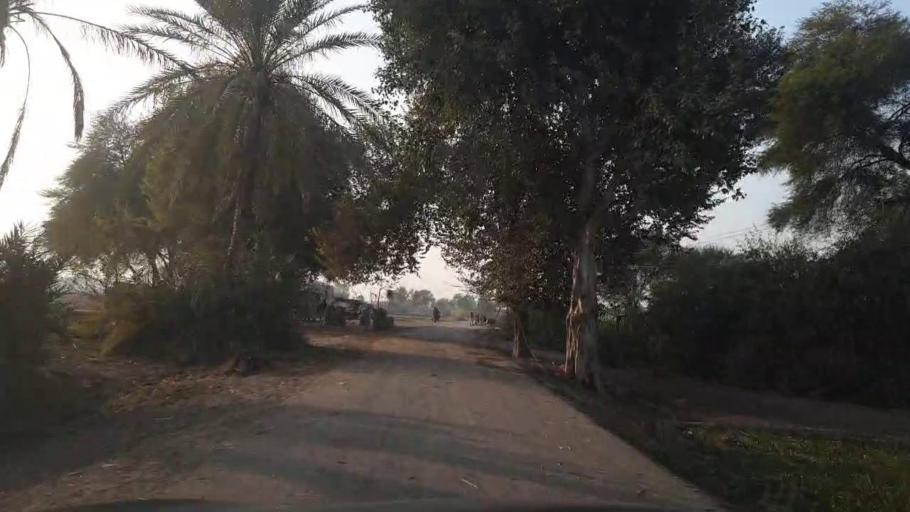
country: PK
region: Sindh
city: Ubauro
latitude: 28.3313
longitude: 69.7726
